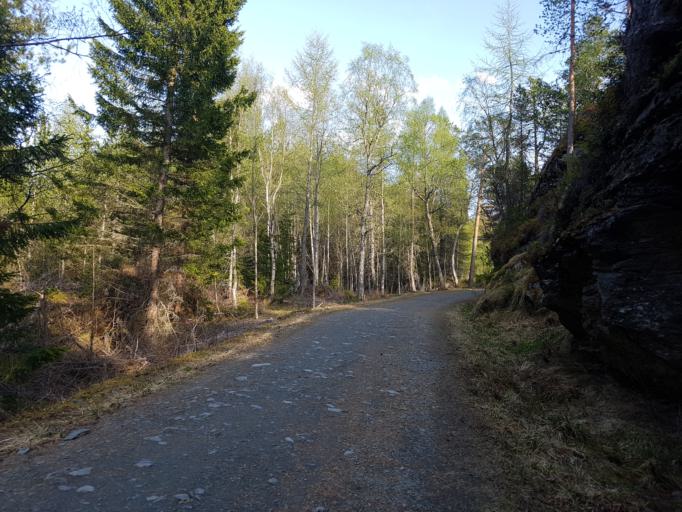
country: NO
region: Sor-Trondelag
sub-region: Trondheim
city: Trondheim
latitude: 63.4401
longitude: 10.3346
